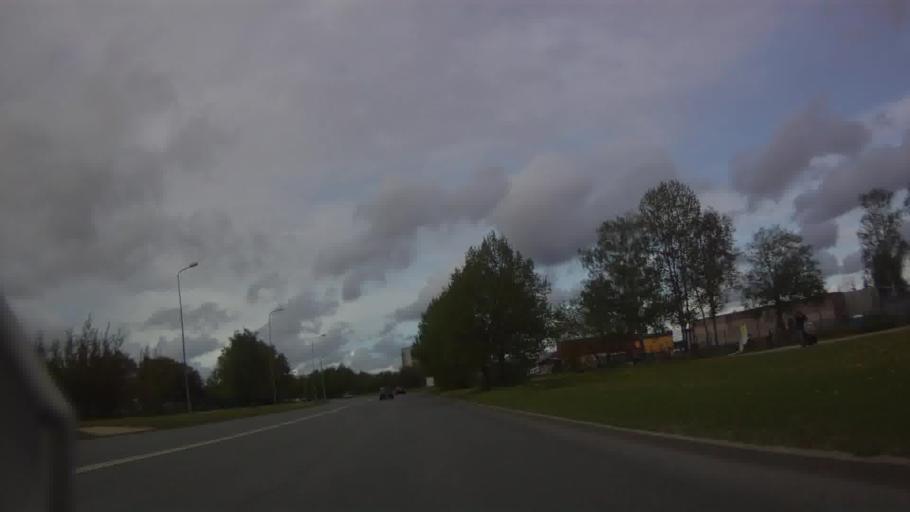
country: LV
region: Stopini
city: Ulbroka
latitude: 56.9551
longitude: 24.2254
